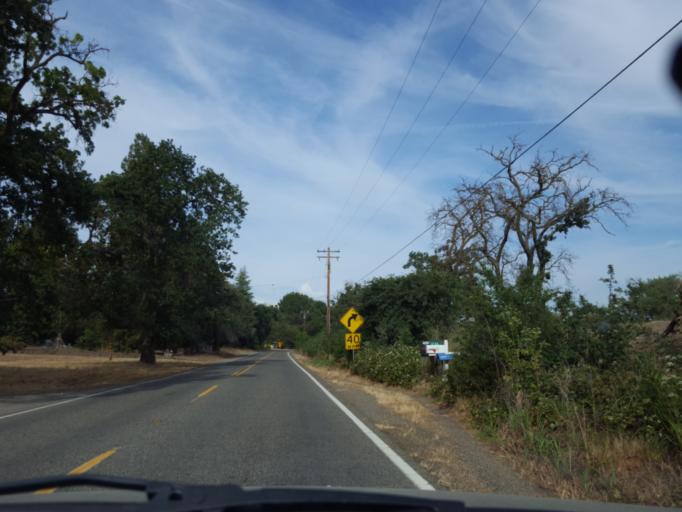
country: US
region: California
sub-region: Merced County
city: Merced
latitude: 37.5220
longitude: -120.4092
